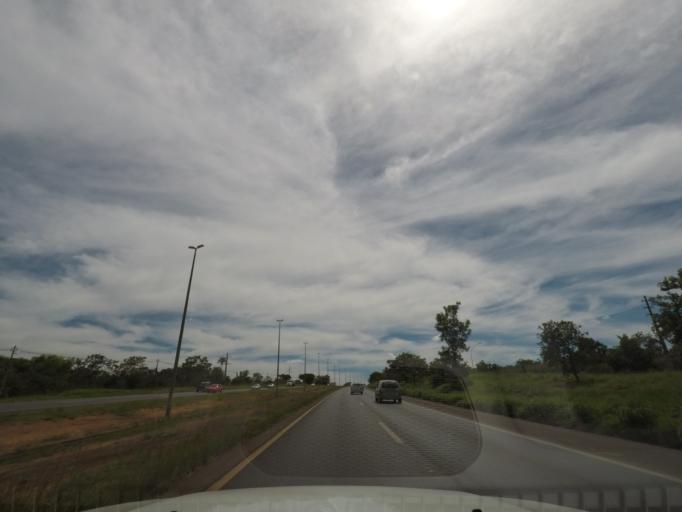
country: BR
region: Goias
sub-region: Planaltina
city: Planaltina
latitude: -15.5950
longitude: -47.6664
